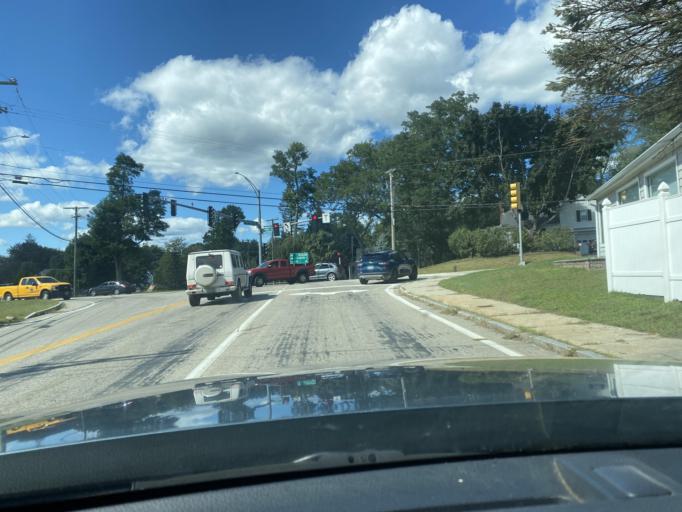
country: US
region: New Hampshire
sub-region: Rockingham County
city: Portsmouth
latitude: 43.0575
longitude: -70.7824
